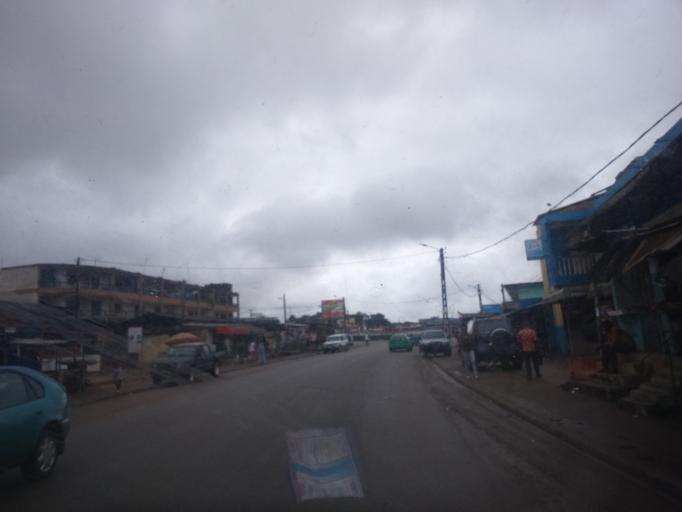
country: CI
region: Sud-Comoe
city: Bonoua
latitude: 5.2699
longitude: -3.5969
